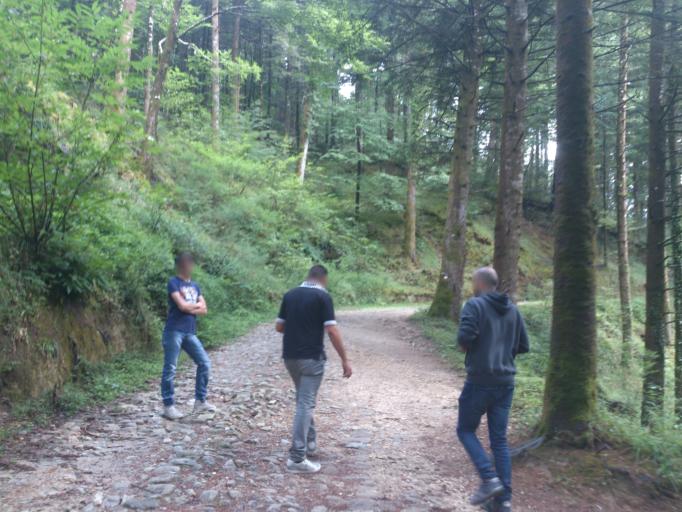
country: IT
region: Calabria
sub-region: Provincia di Vibo-Valentia
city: Serra San Bruno
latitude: 38.5525
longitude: 16.3110
